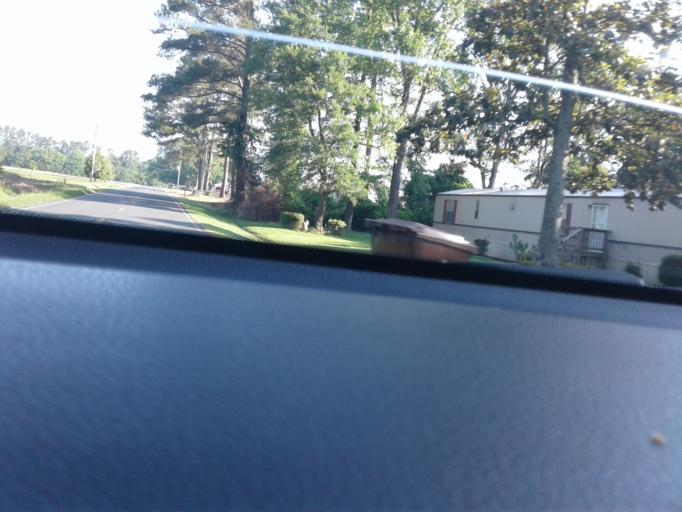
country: US
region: North Carolina
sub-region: Harnett County
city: Dunn
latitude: 35.3414
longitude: -78.5773
